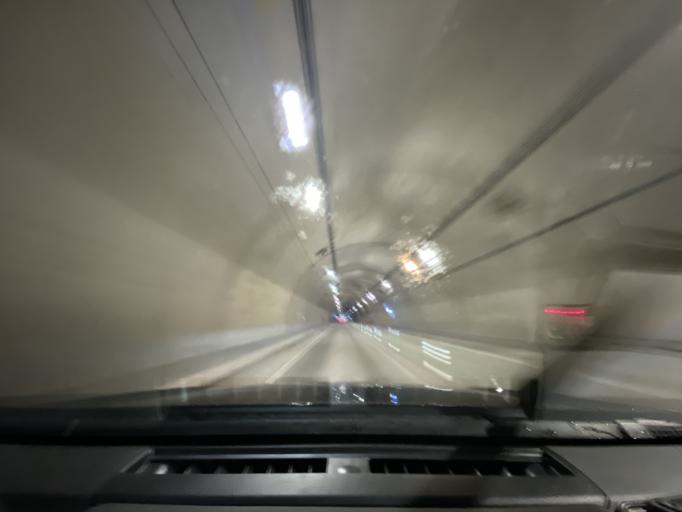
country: JP
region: Hokkaido
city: Kitami
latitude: 43.7847
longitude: 143.9023
